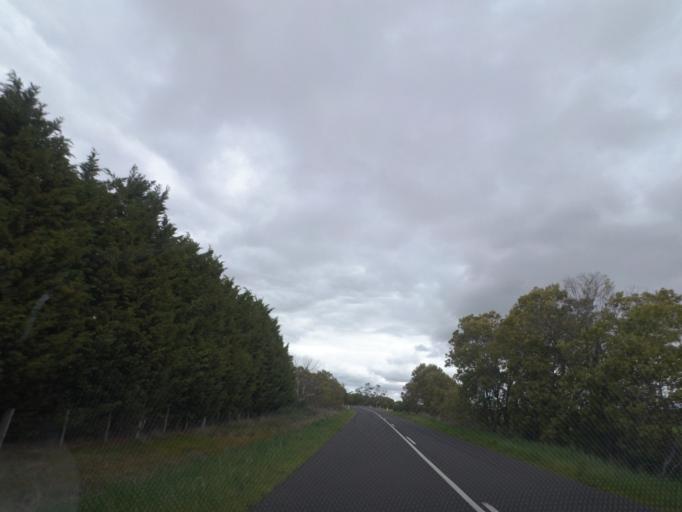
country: AU
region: Victoria
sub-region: Hume
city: Sunbury
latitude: -37.3785
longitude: 144.8268
